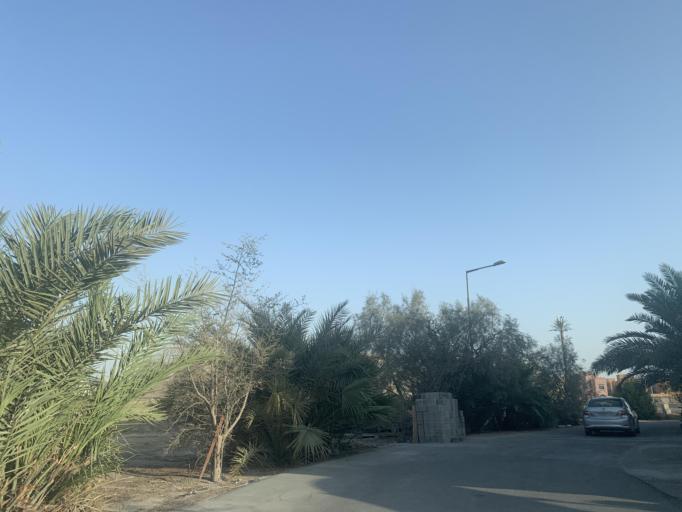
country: BH
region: Manama
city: Jidd Hafs
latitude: 26.2113
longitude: 50.5251
